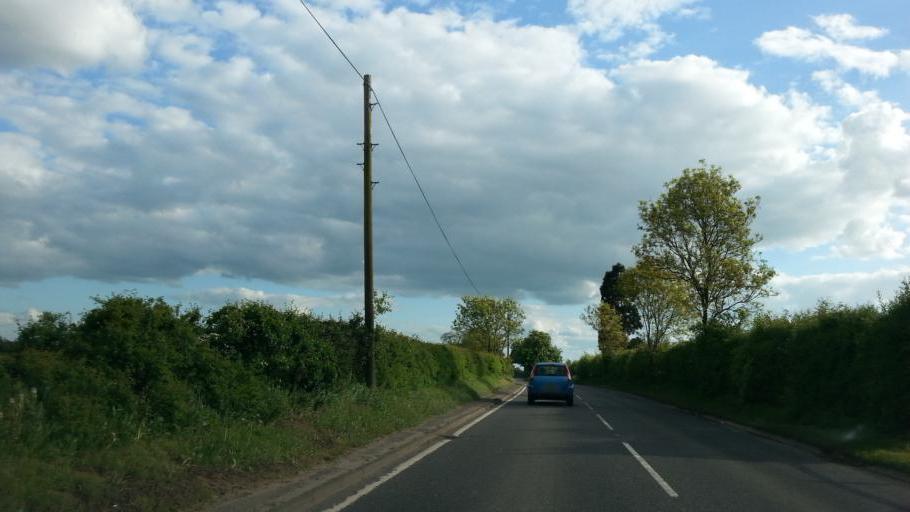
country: GB
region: England
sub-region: Nottinghamshire
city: South Collingham
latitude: 53.1199
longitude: -0.7709
